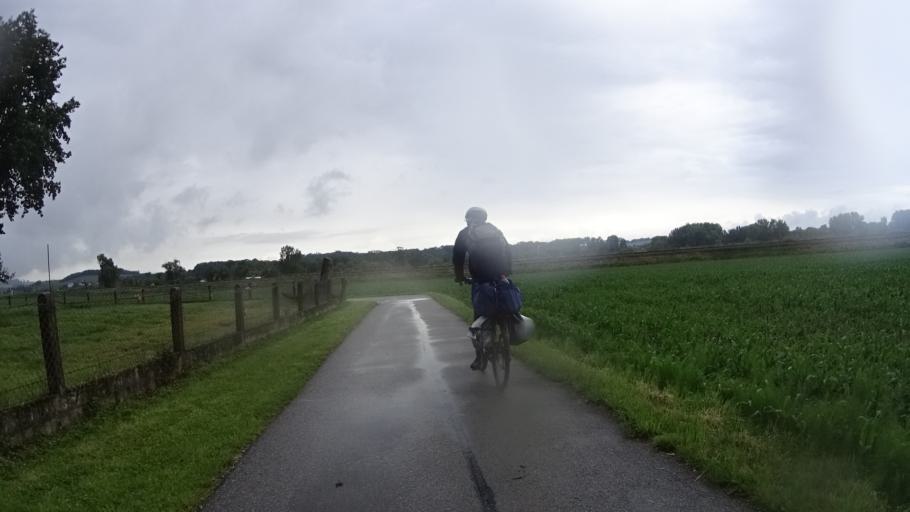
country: DE
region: Bavaria
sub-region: Lower Bavaria
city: Pocking
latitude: 48.4062
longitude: 13.2911
